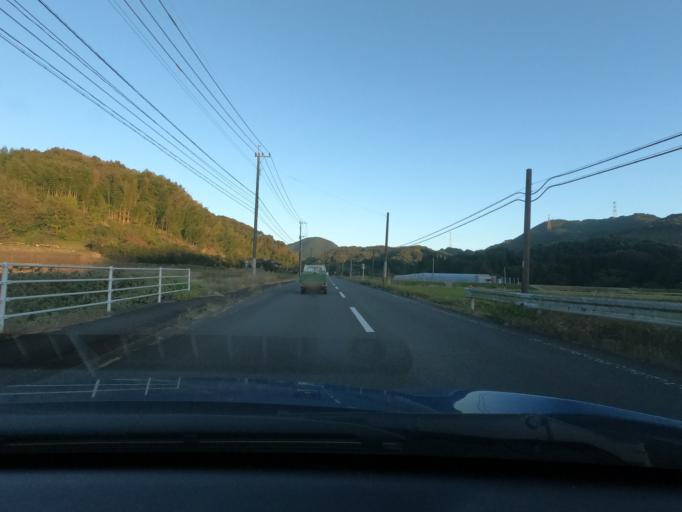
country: JP
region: Kagoshima
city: Satsumasendai
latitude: 31.7906
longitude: 130.4626
